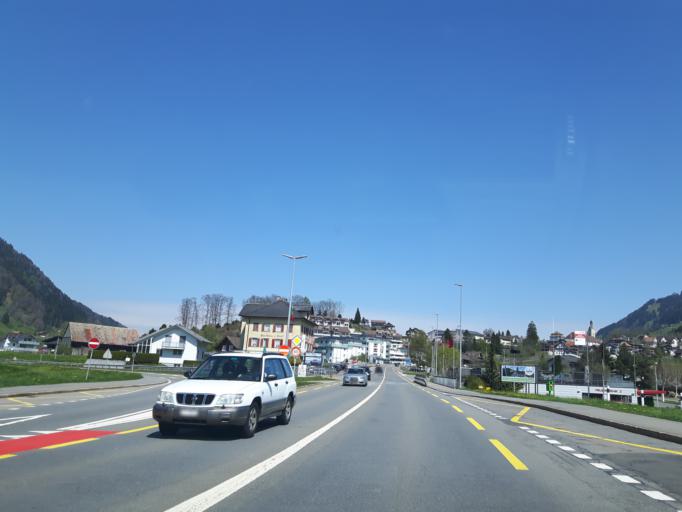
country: CH
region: Schwyz
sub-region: Bezirk Schwyz
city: Sattel
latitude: 47.0781
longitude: 8.6338
